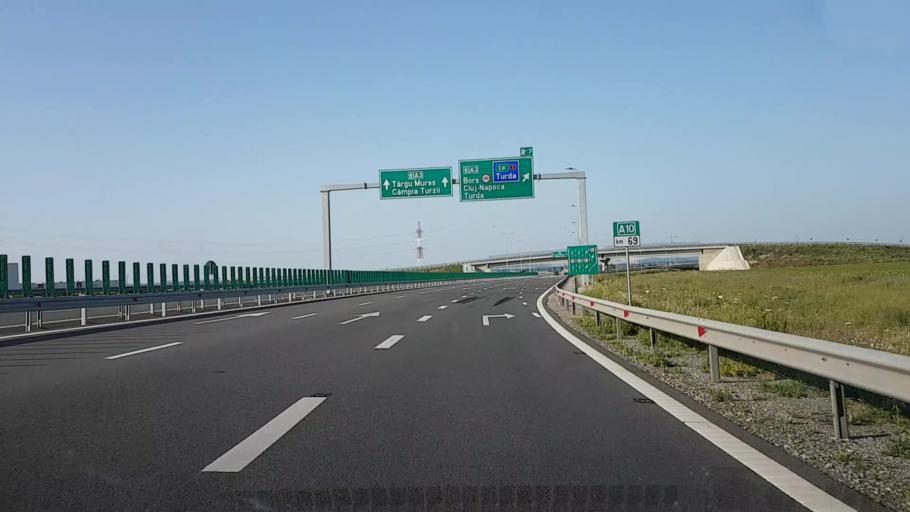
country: RO
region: Cluj
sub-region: Comuna Mihai Viteazu
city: Mihai Viteazu
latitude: 46.5157
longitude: 23.7844
